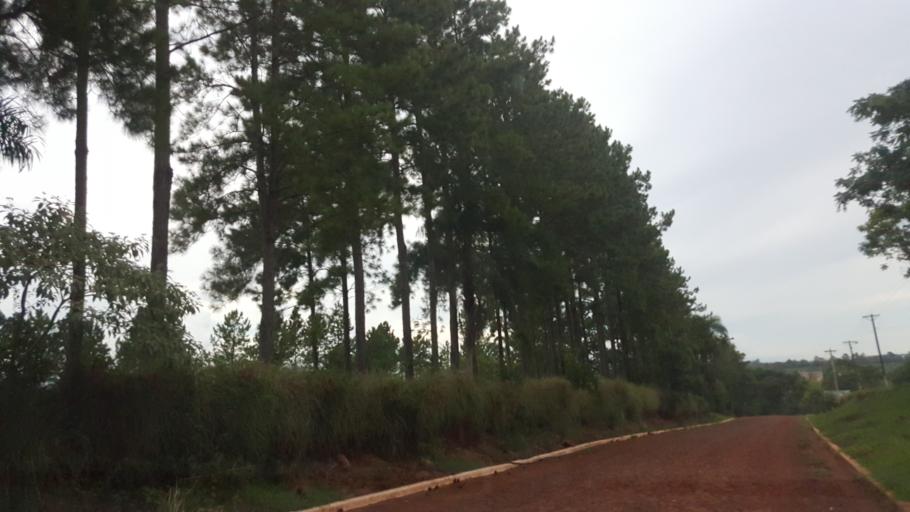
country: AR
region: Misiones
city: Santo Pipo
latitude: -27.1079
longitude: -55.3751
